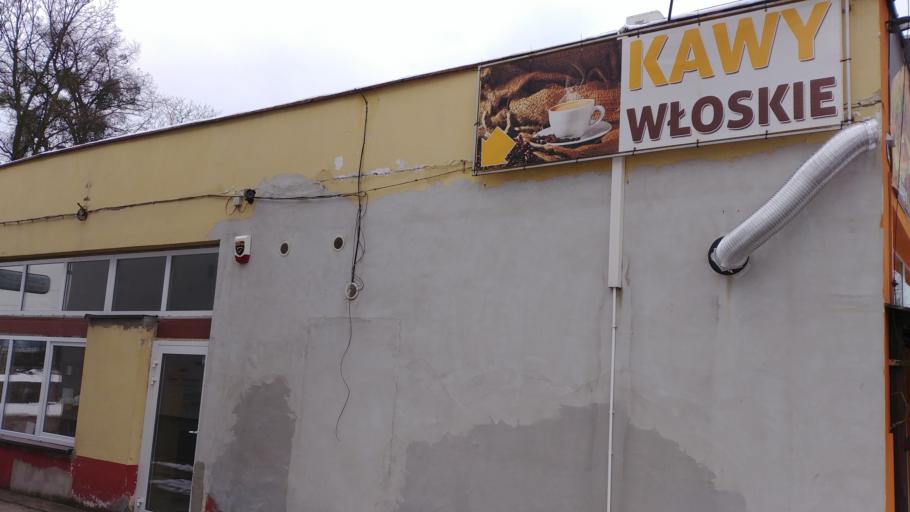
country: PL
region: Silesian Voivodeship
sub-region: Powiat tarnogorski
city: Tarnowskie Gory
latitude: 50.4758
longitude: 18.7970
